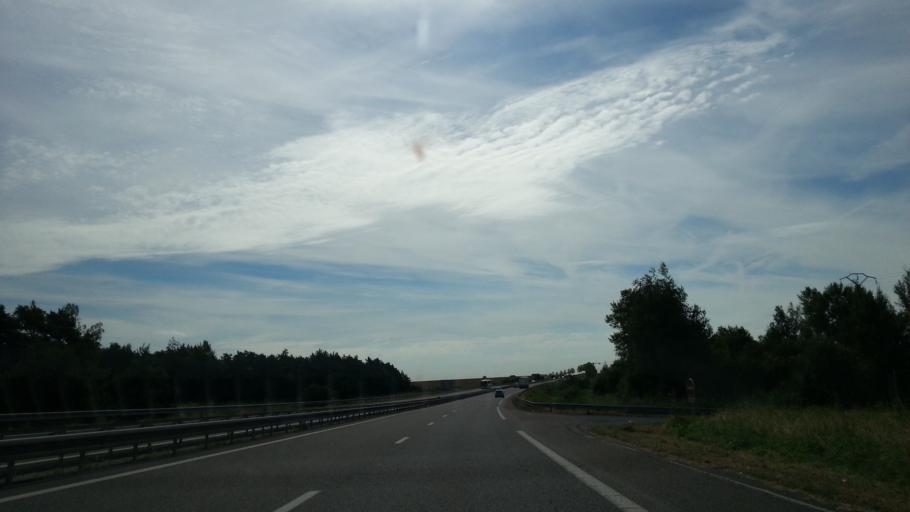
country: FR
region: Champagne-Ardenne
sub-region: Departement de la Marne
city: Fagnieres
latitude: 49.0393
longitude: 4.3450
